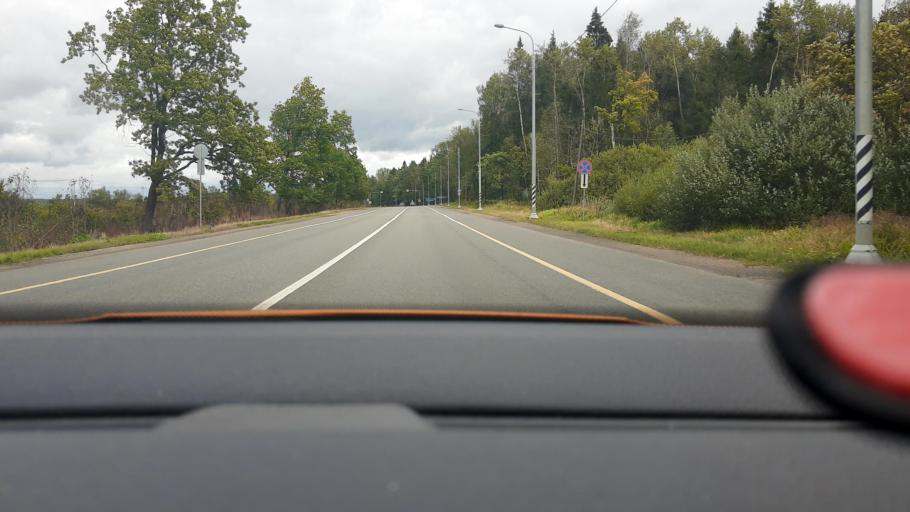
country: RU
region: Moskovskaya
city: Kostino
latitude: 56.0289
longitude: 37.9589
